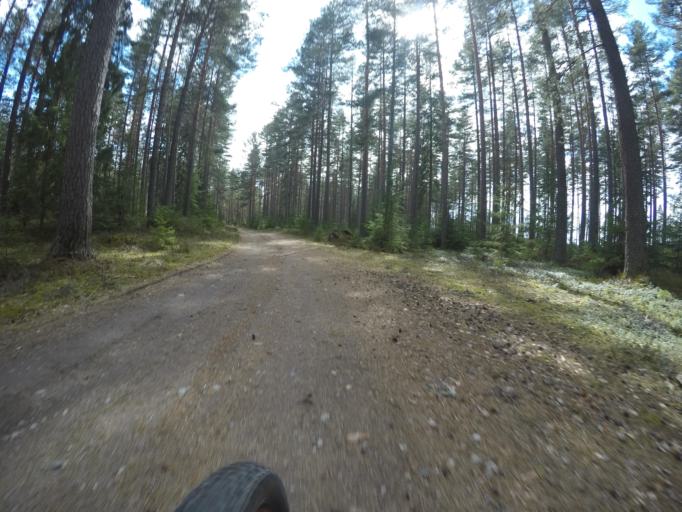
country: SE
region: Vaestmanland
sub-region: Kungsors Kommun
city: Kungsoer
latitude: 59.3445
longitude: 16.1076
